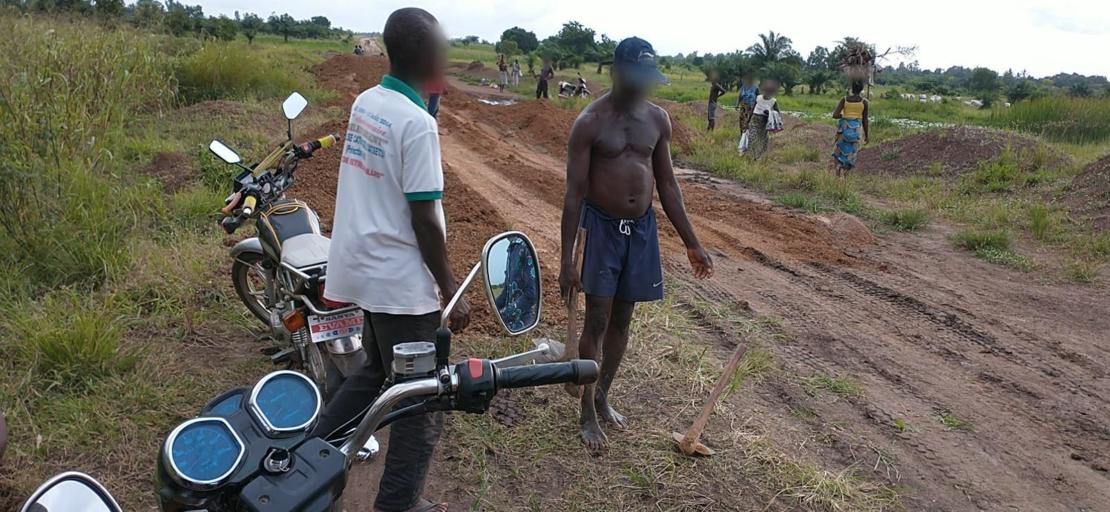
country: TG
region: Maritime
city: Vogan
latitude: 6.4442
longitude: 1.5294
